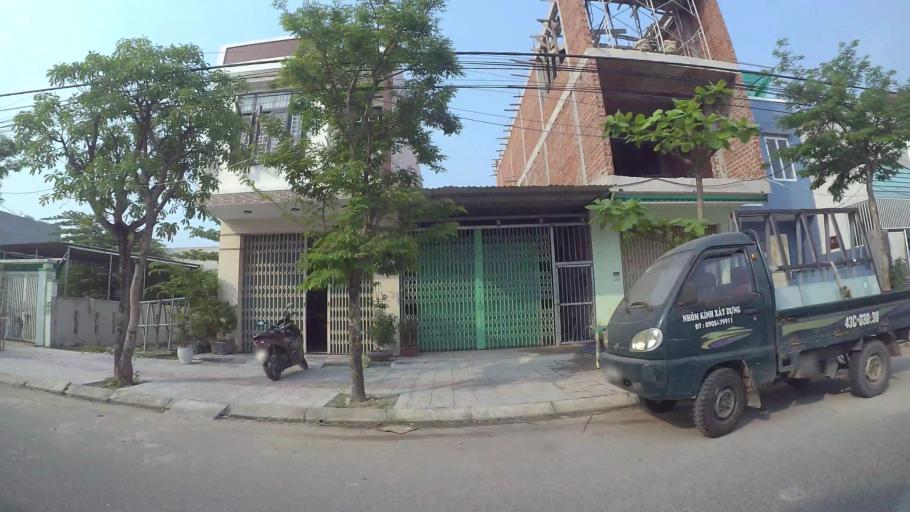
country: VN
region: Da Nang
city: Cam Le
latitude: 16.0085
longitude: 108.2232
